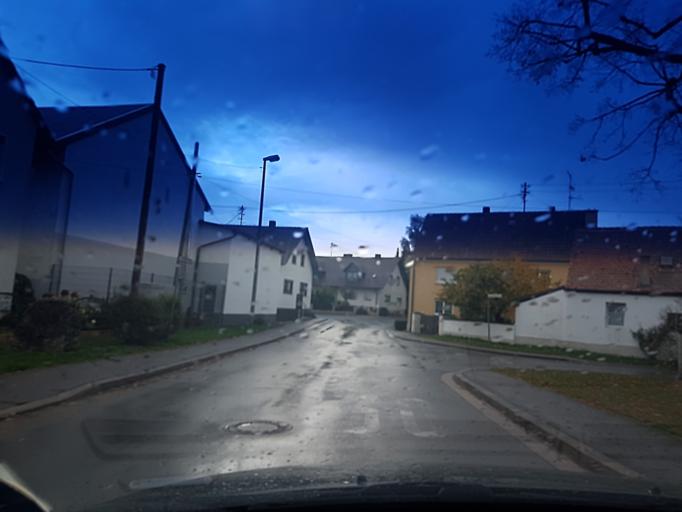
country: DE
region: Bavaria
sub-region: Upper Franconia
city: Pettstadt
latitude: 49.8069
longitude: 10.9554
